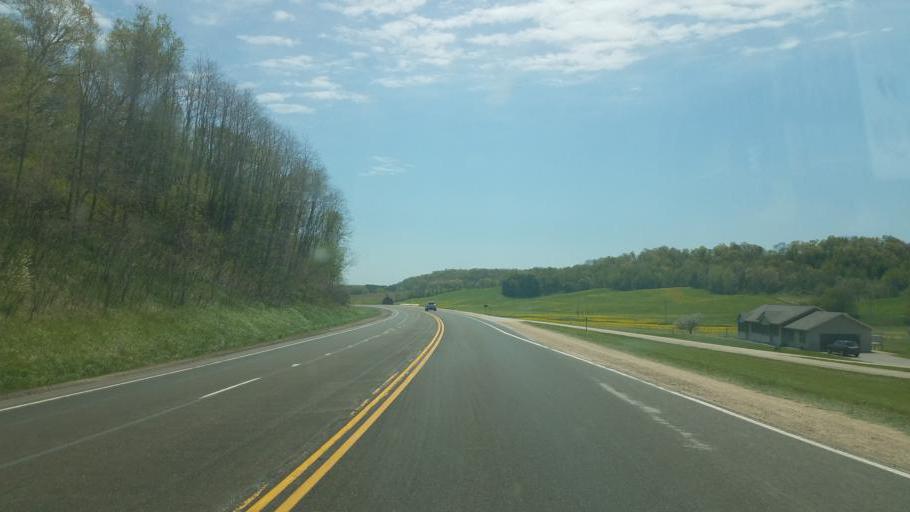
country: US
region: Wisconsin
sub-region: Monroe County
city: Tomah
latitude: 43.8795
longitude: -90.4813
